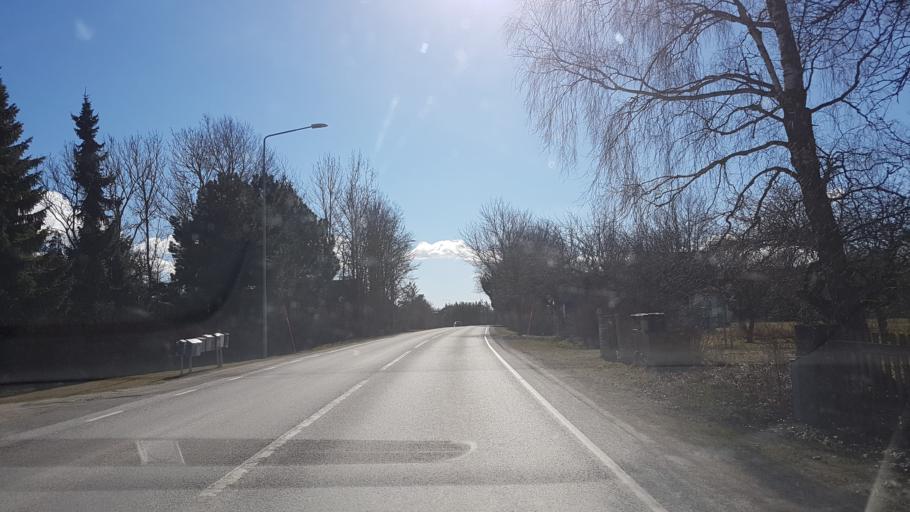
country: SE
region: Gotland
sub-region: Gotland
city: Visby
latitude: 57.5201
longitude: 18.4428
